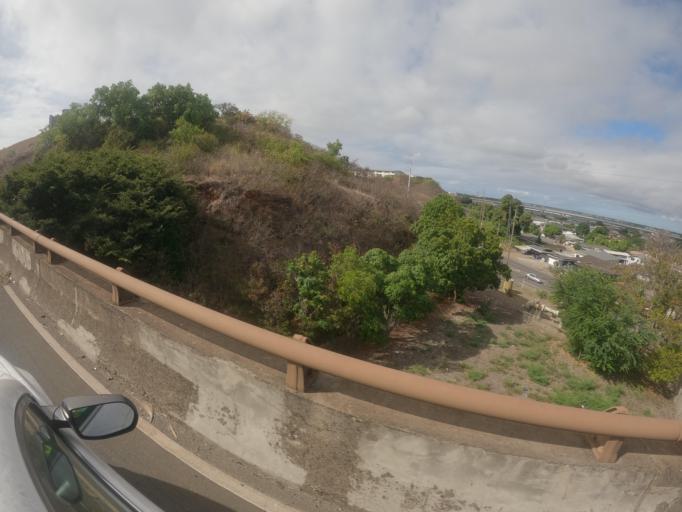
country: US
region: Hawaii
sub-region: Honolulu County
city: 'Aiea
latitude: 21.3902
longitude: -157.9459
